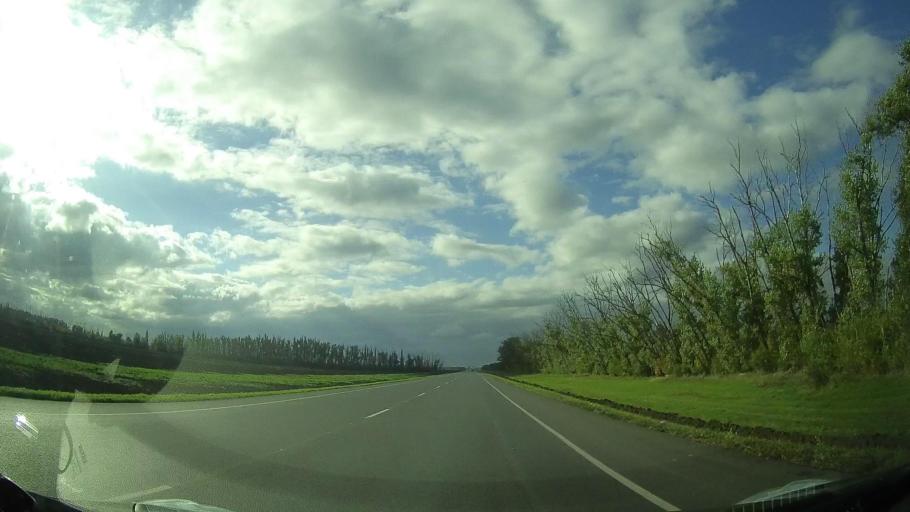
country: RU
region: Rostov
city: Tselina
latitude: 46.5307
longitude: 40.9434
